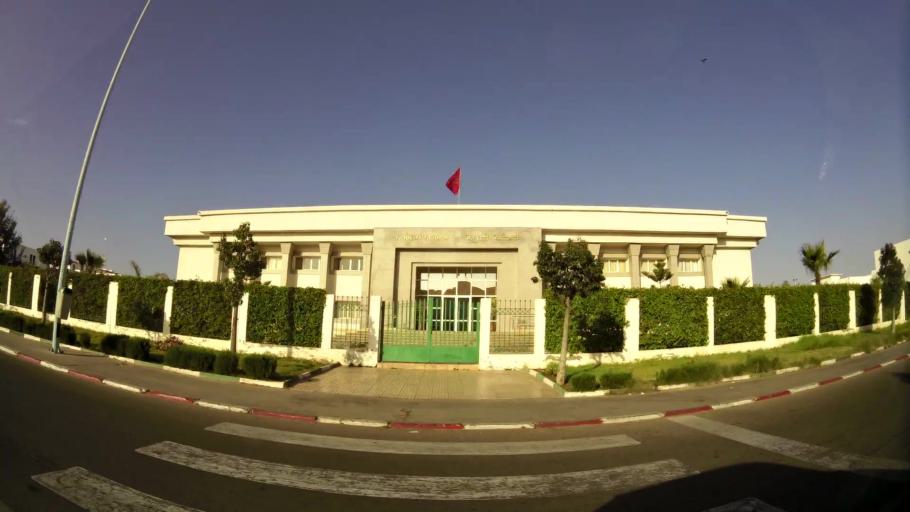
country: MA
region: Oued ed Dahab-Lagouira
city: Dakhla
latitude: 30.4043
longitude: -9.5789
